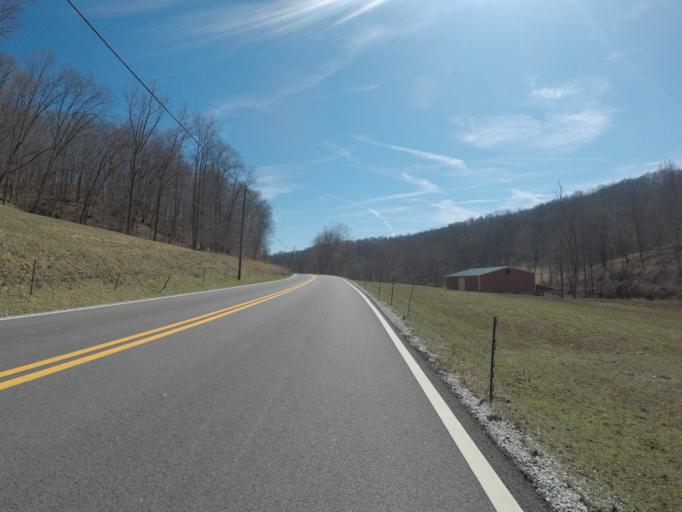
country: US
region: Ohio
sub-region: Lawrence County
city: Burlington
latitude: 38.4535
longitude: -82.5200
